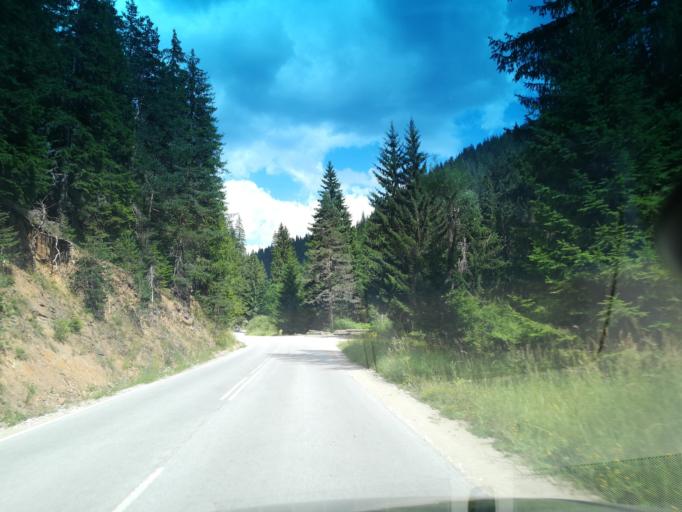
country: BG
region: Smolyan
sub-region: Obshtina Chepelare
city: Chepelare
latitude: 41.6620
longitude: 24.6471
